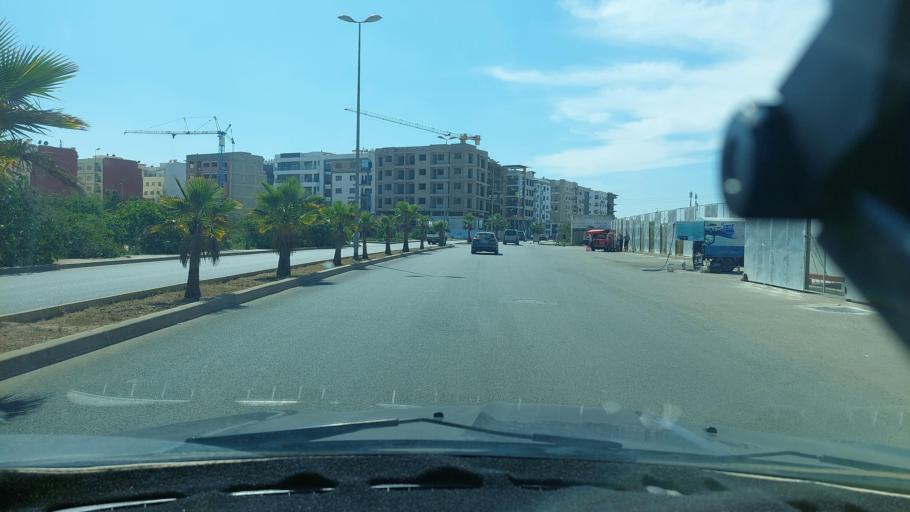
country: MA
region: Grand Casablanca
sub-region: Casablanca
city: Casablanca
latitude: 33.5295
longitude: -7.6057
